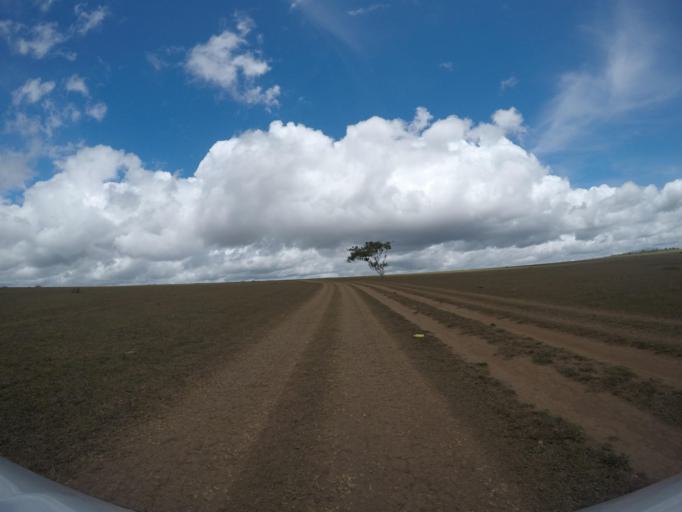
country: TL
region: Lautem
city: Lospalos
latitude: -8.4610
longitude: 126.9845
